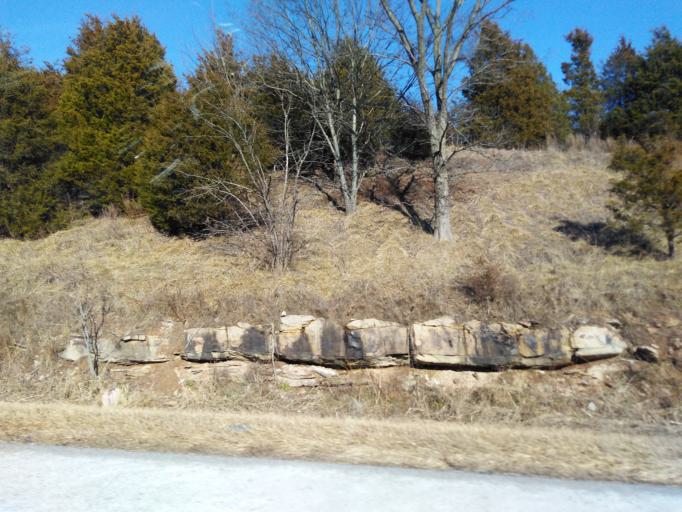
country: US
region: Illinois
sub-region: Johnson County
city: Goreville
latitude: 37.5165
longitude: -88.9106
